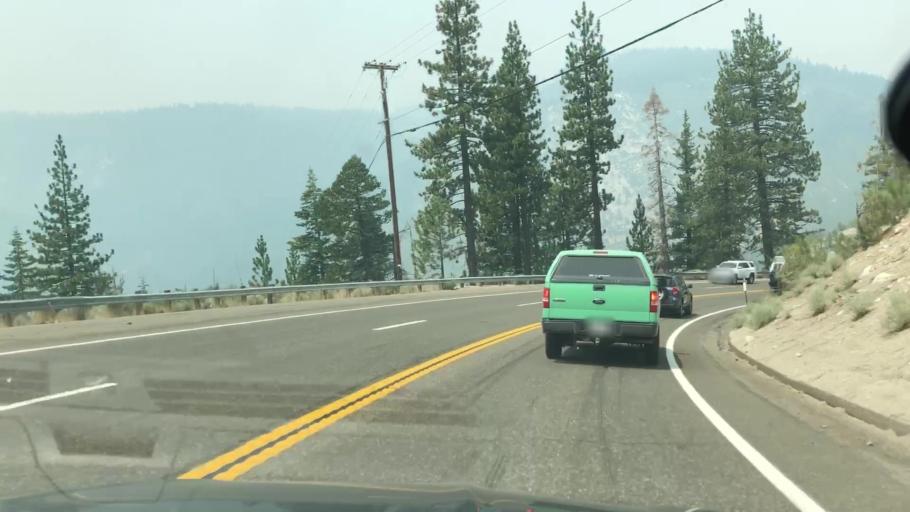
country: US
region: California
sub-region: El Dorado County
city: South Lake Tahoe
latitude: 38.8024
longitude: -120.1216
